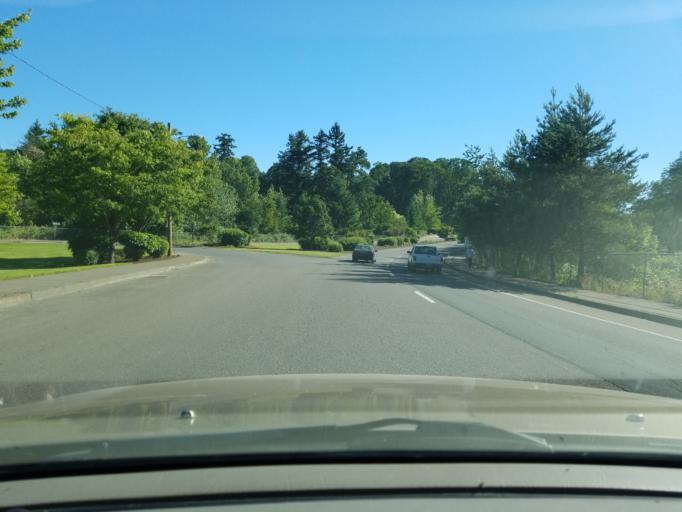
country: US
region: Oregon
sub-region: Yamhill County
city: McMinnville
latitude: 45.2045
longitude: -123.1996
